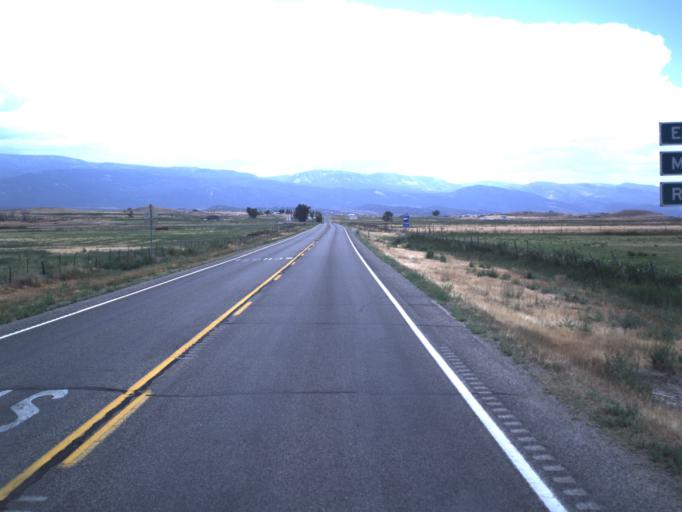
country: US
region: Utah
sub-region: Sanpete County
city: Moroni
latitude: 39.5227
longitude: -111.5754
